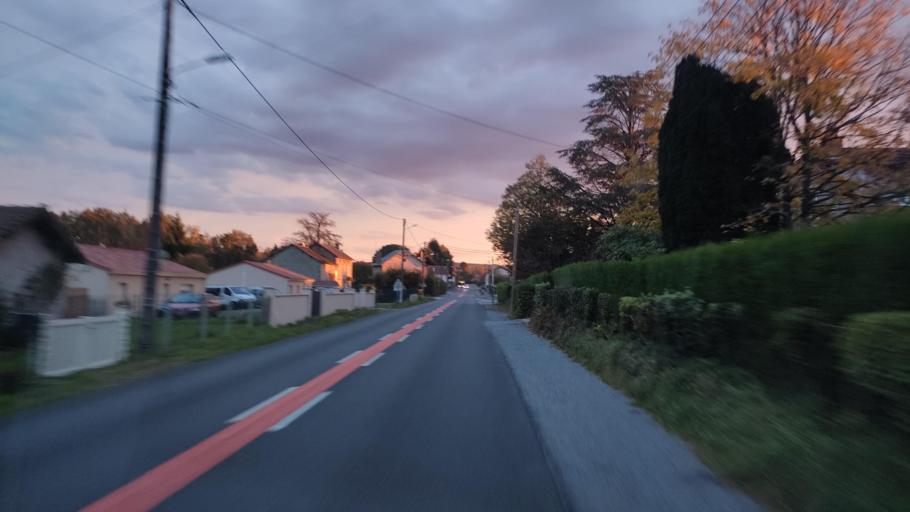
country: FR
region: Limousin
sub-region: Departement de la Haute-Vienne
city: Rilhac-Rancon
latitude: 45.9219
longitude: 1.3409
